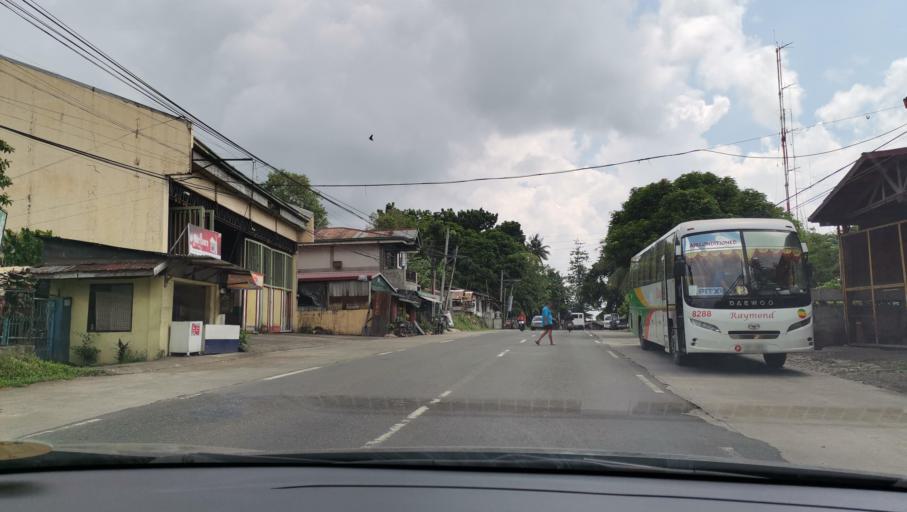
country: PH
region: Calabarzon
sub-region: Province of Quezon
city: Calauag
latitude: 13.9545
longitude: 122.2893
